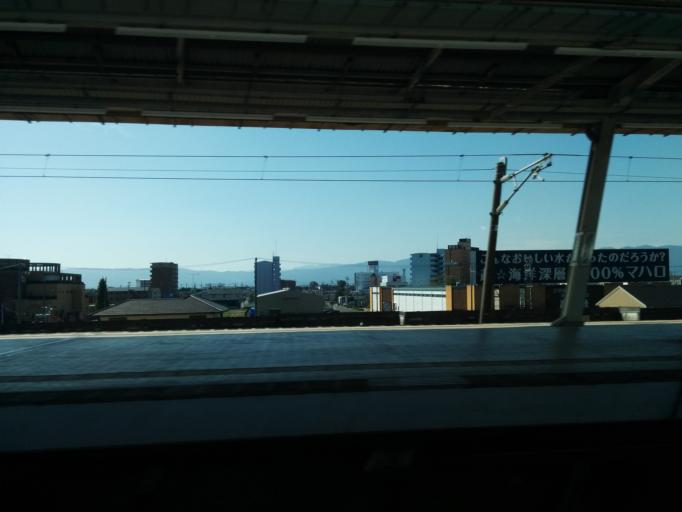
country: JP
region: Aichi
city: Sobue
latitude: 35.3143
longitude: 136.6873
